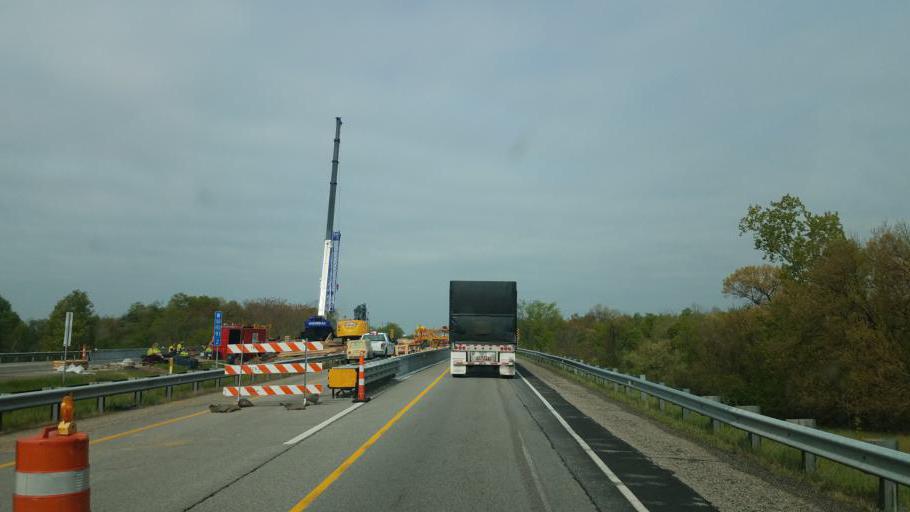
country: US
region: Indiana
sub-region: Elkhart County
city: Simonton Lake
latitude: 41.7314
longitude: -85.9821
